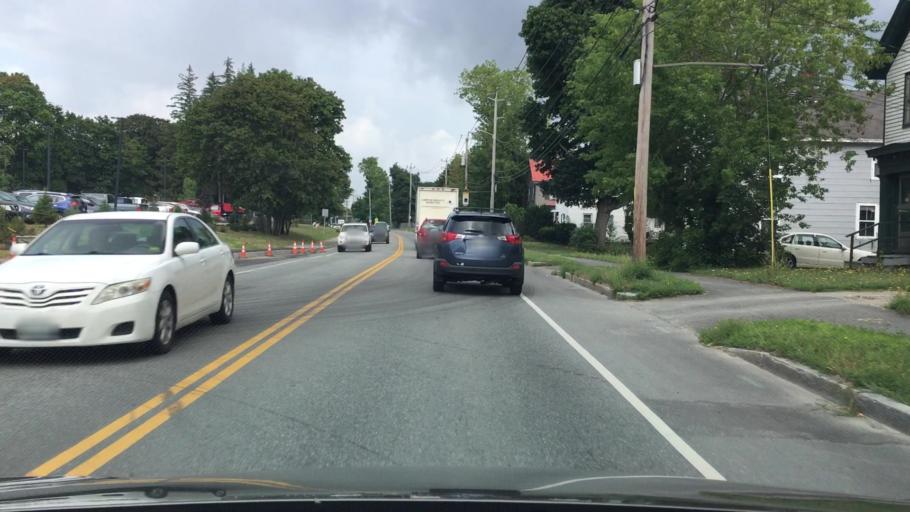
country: US
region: Maine
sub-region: Penobscot County
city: Bangor
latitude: 44.8149
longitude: -68.7714
